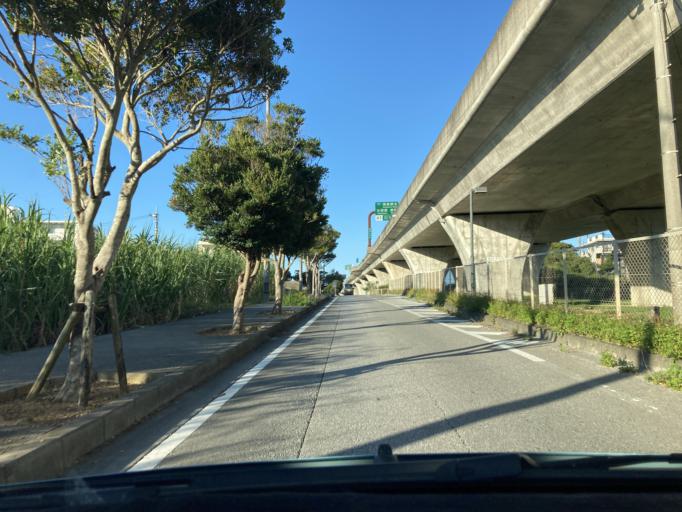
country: JP
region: Okinawa
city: Tomigusuku
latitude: 26.1891
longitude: 127.7380
